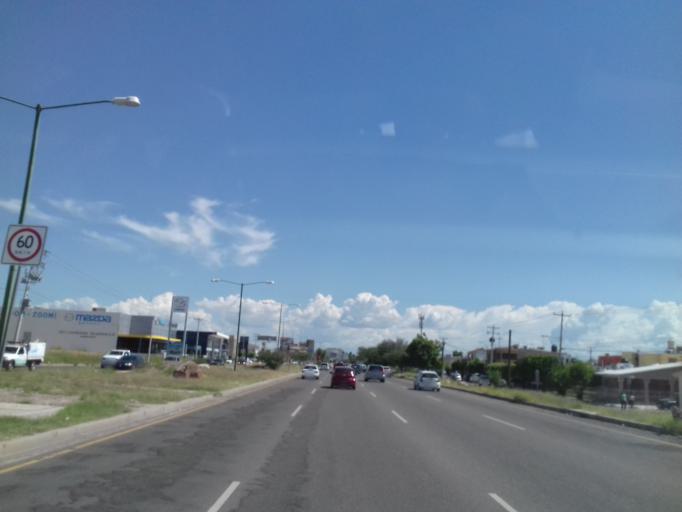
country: MX
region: Sonora
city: Hermosillo
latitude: 29.0851
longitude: -110.9950
